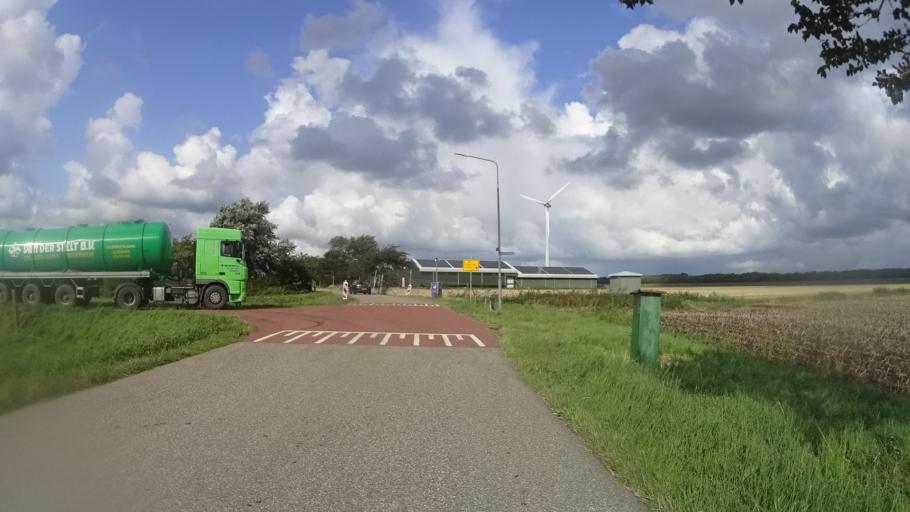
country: NL
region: North Holland
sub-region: Gemeente Schagen
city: Schagen
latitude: 52.8598
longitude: 4.8928
